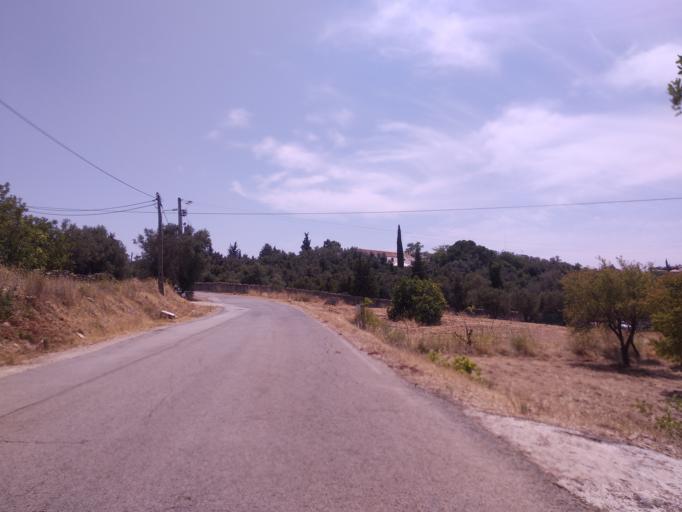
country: PT
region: Faro
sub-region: Faro
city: Santa Barbara de Nexe
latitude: 37.1239
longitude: -7.9391
